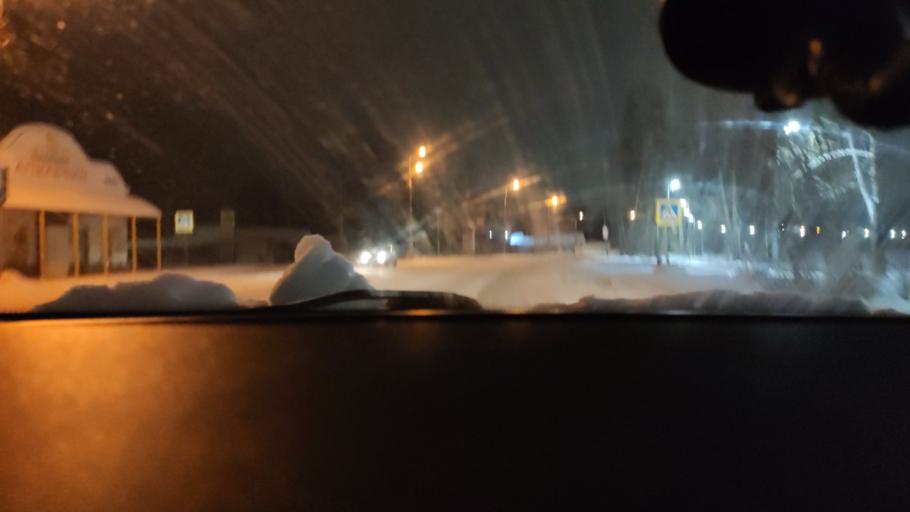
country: RU
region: Perm
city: Krasnokamsk
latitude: 58.0615
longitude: 55.8045
